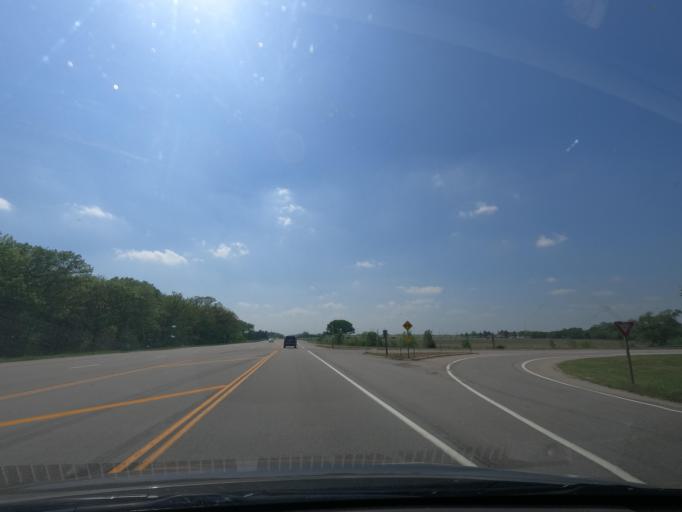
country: US
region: Kansas
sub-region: Butler County
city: El Dorado
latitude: 37.6796
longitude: -96.7823
